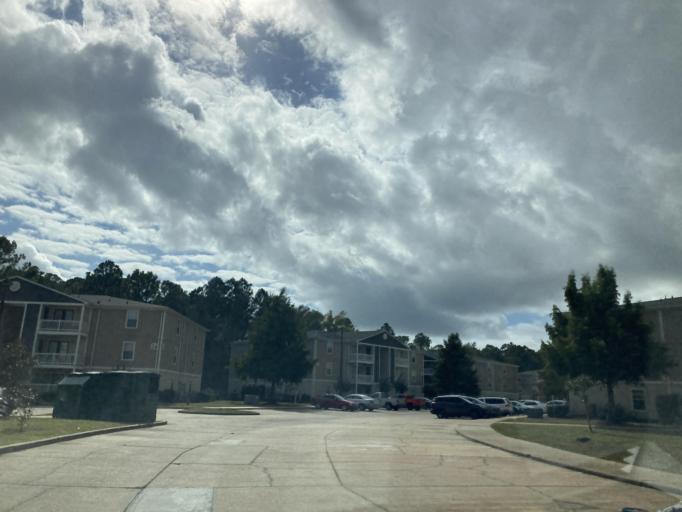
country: US
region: Mississippi
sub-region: Jackson County
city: Gulf Hills
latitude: 30.4367
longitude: -88.8342
